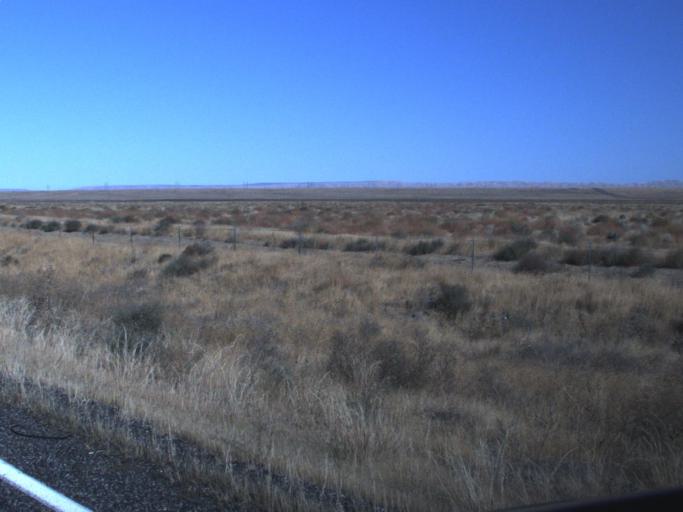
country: US
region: Washington
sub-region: Grant County
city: Desert Aire
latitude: 46.5231
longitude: -119.6756
